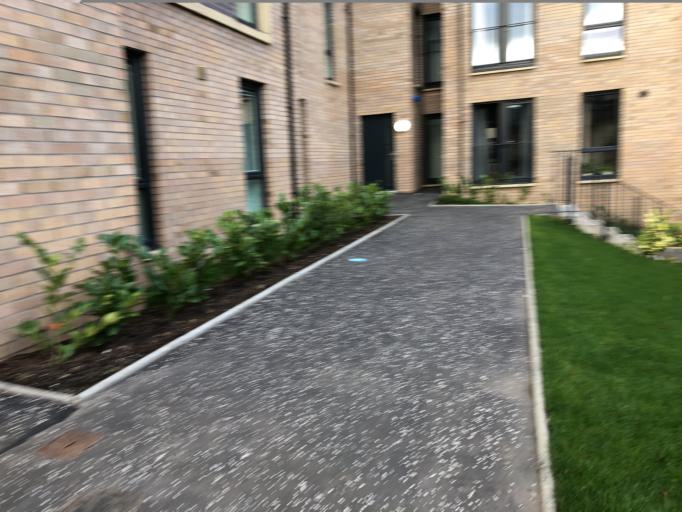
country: GB
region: Scotland
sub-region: West Lothian
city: Seafield
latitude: 55.9559
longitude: -3.1658
